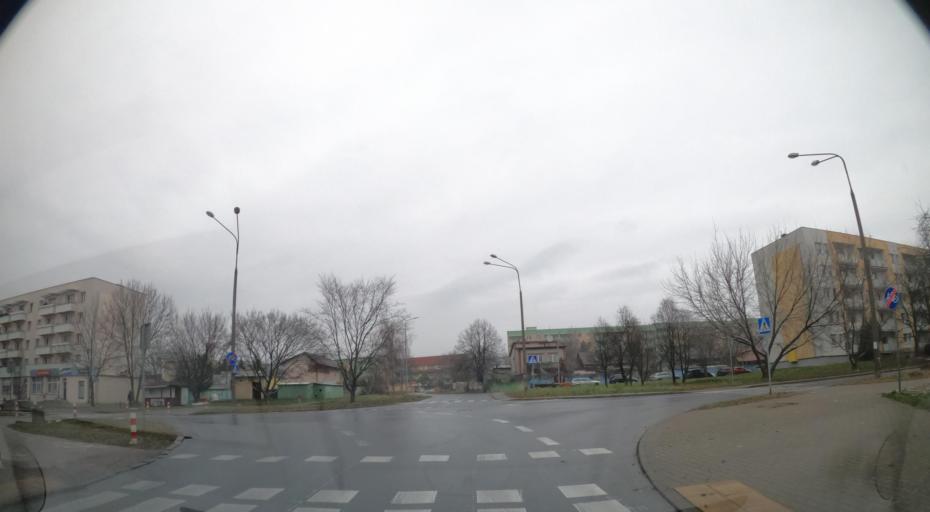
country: PL
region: Masovian Voivodeship
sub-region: Powiat radomski
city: Trablice
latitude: 51.3711
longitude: 21.1347
